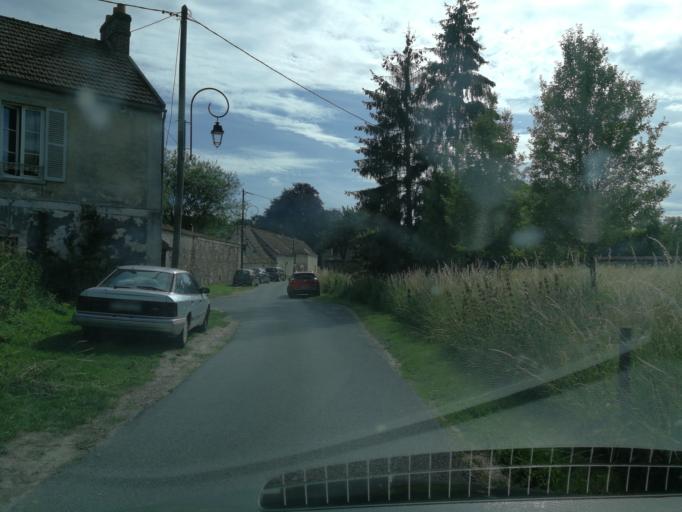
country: FR
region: Ile-de-France
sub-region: Departement de l'Essonne
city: Fontenay-les-Briis
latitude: 48.6011
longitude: 2.1501
